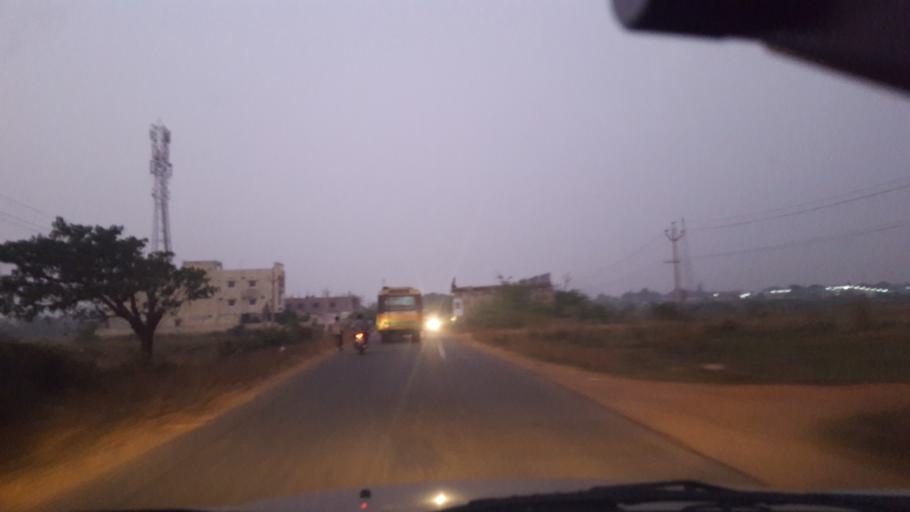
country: IN
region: Andhra Pradesh
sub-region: Srikakulam
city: Palasa
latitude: 18.7518
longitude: 84.4163
